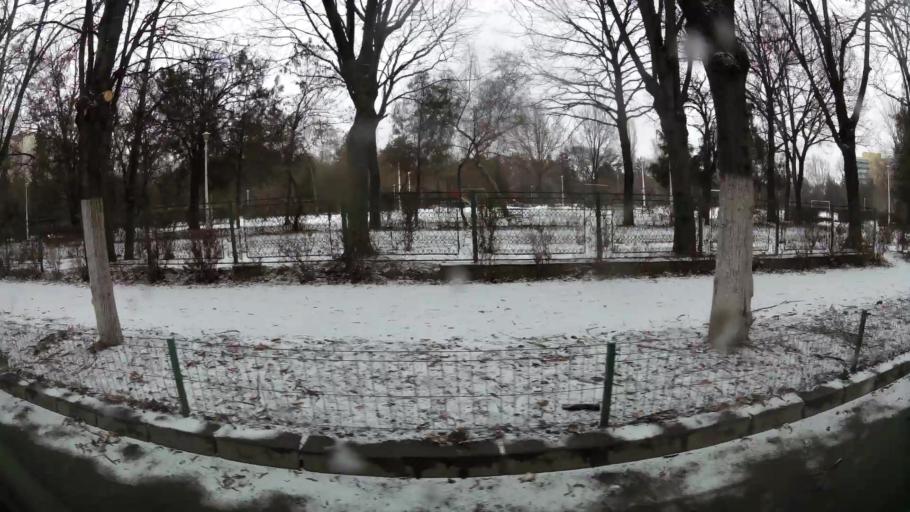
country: RO
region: Prahova
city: Ploiesti
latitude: 44.9562
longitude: 26.0079
